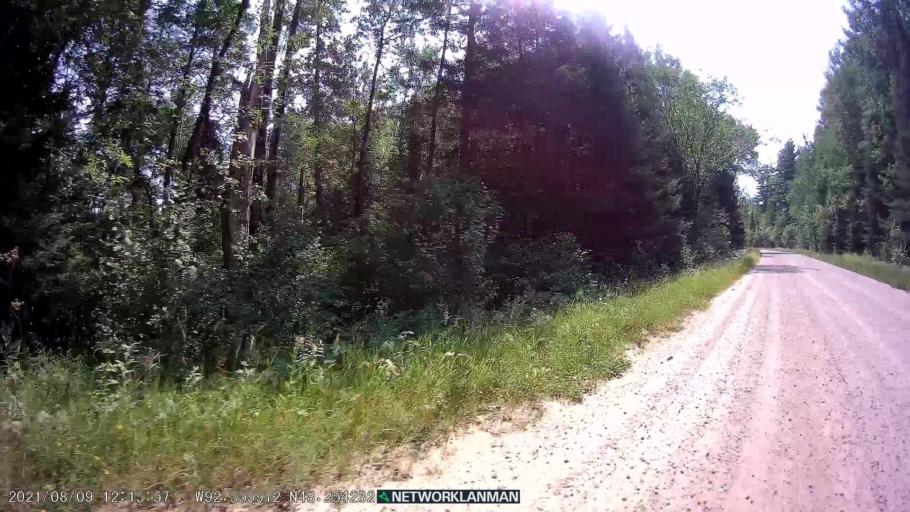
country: US
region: Minnesota
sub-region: Saint Louis County
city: Parkville
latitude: 48.2541
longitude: -92.5599
